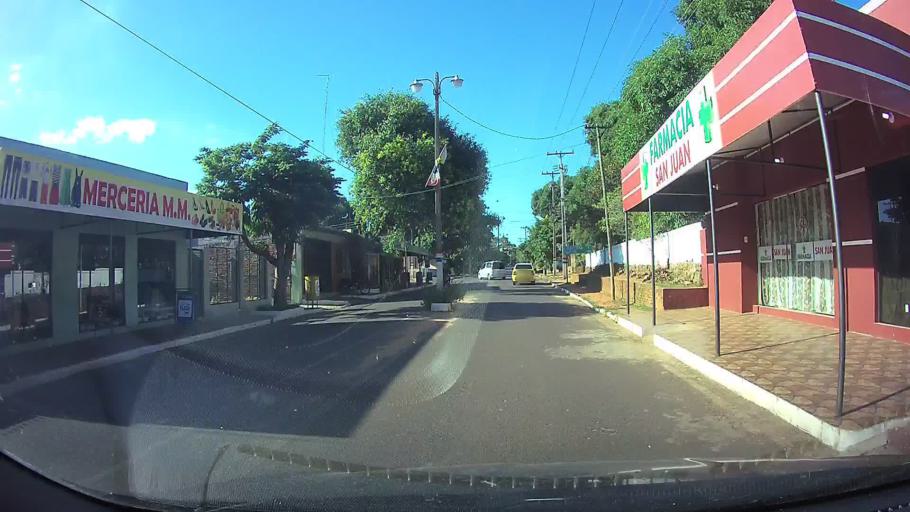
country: PY
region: Cordillera
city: Atyra
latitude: -25.2849
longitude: -57.1712
